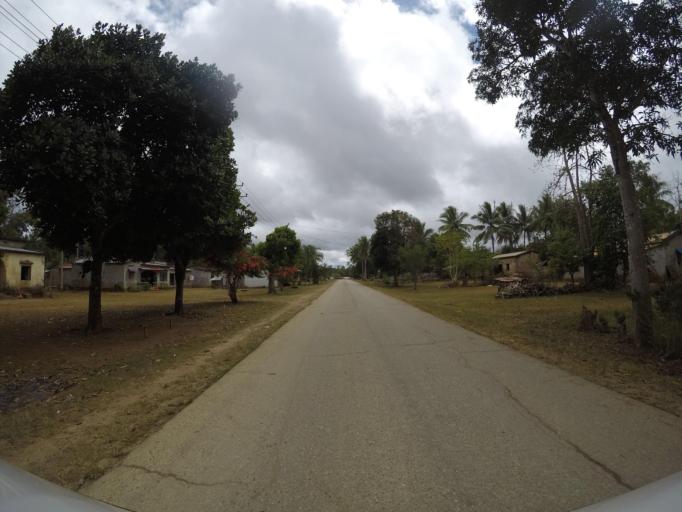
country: TL
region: Lautem
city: Lospalos
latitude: -8.4716
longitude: 126.9931
